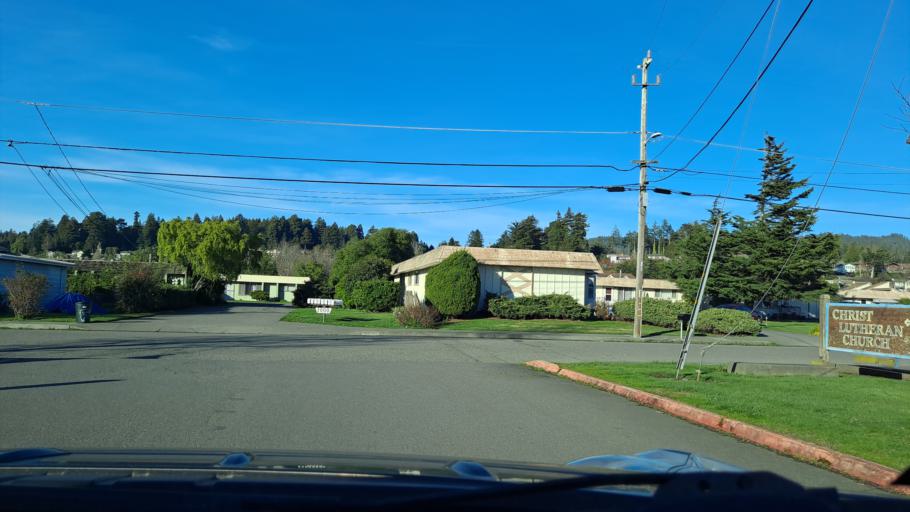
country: US
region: California
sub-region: Humboldt County
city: Fortuna
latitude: 40.5919
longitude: -124.1446
